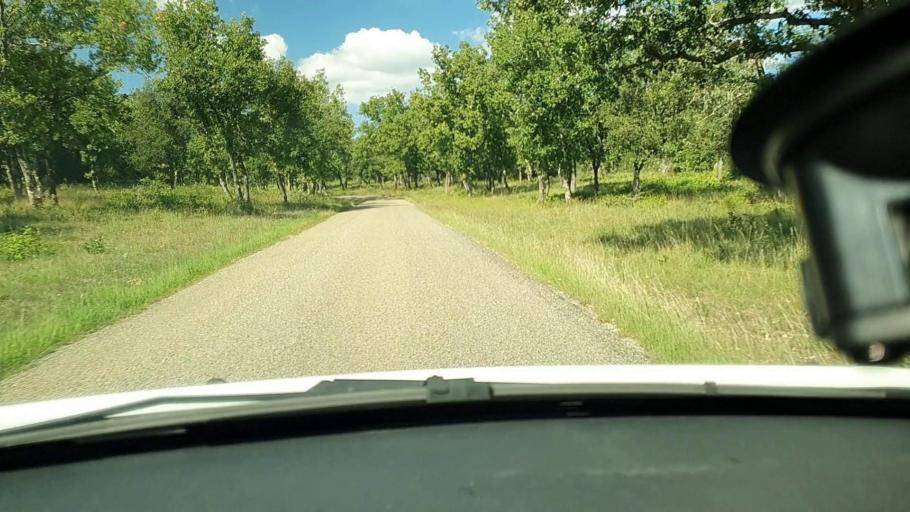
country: FR
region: Languedoc-Roussillon
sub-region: Departement du Gard
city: Goudargues
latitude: 44.1581
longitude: 4.4093
